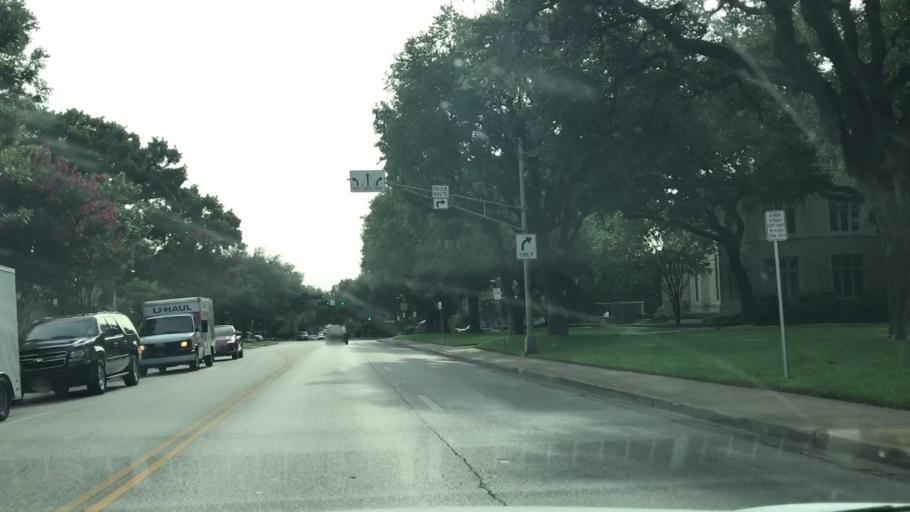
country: US
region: Texas
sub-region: Dallas County
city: Highland Park
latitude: 32.8366
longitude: -96.7857
